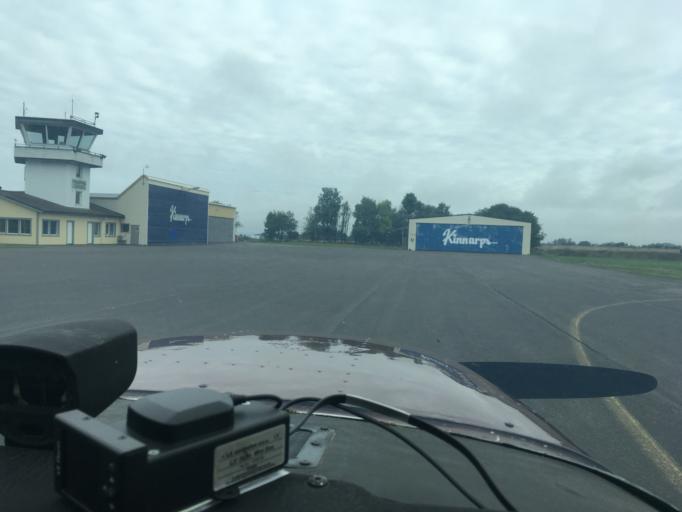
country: SE
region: Vaestra Goetaland
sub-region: Falkopings Kommun
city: Falkoeping
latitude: 58.1754
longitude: 13.5912
